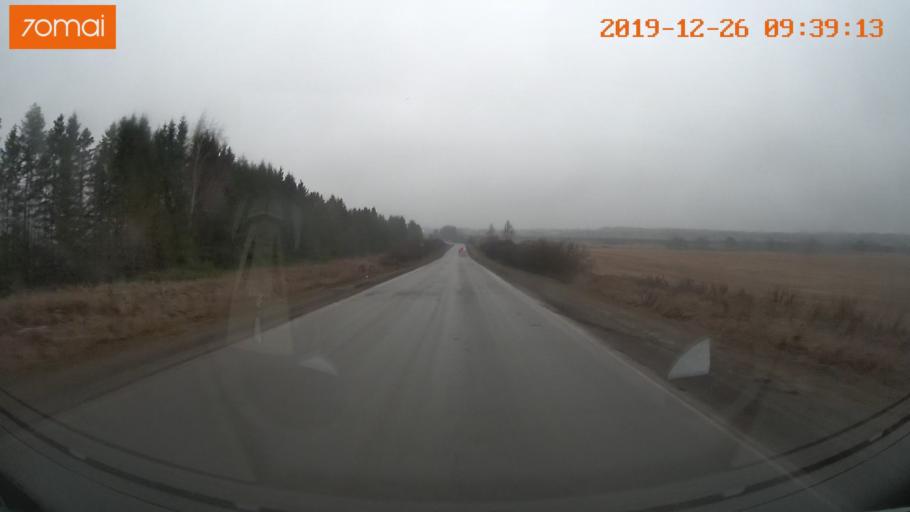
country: RU
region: Vologda
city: Vologda
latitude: 59.1523
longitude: 40.0290
